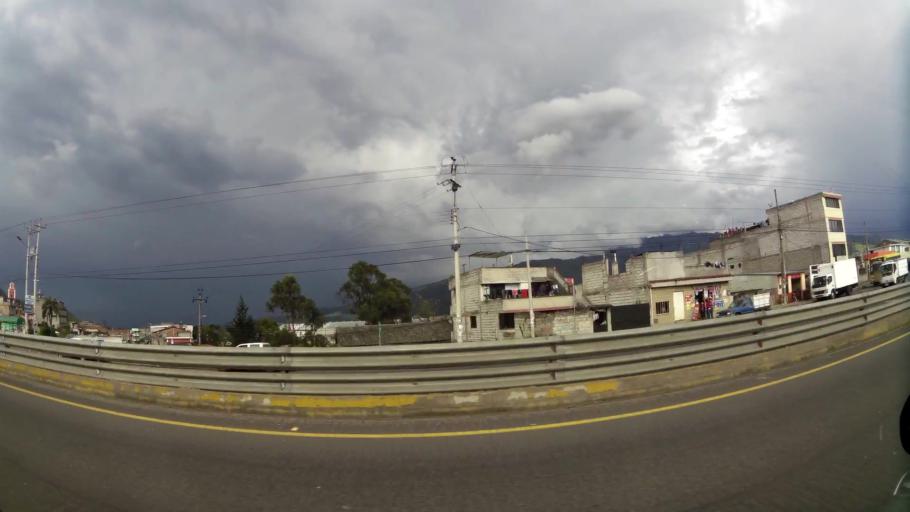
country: EC
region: Pichincha
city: Machachi
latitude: -0.4067
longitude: -78.5468
